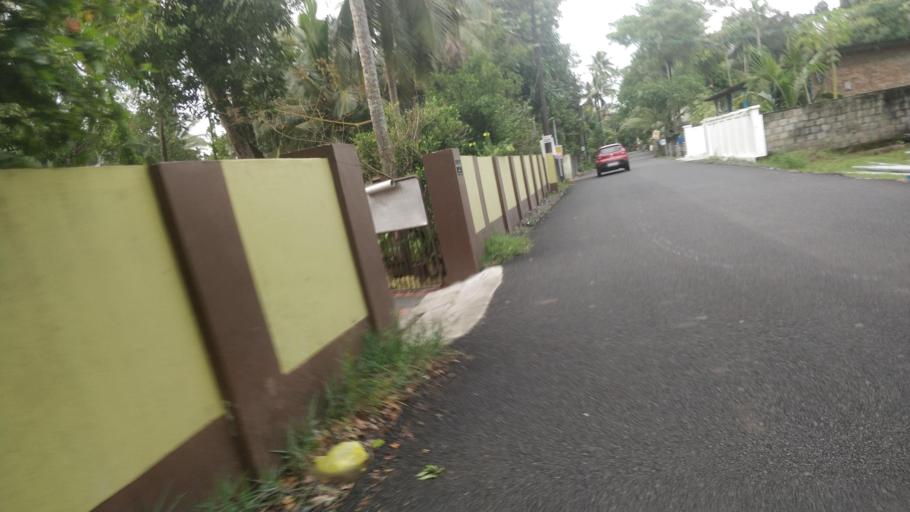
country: IN
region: Kerala
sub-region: Alappuzha
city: Shertallai
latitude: 9.6799
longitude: 76.3513
